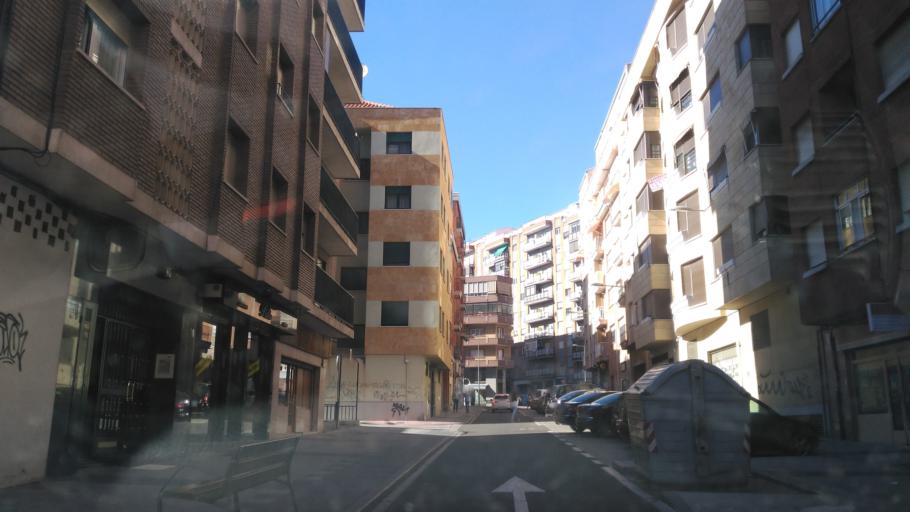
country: ES
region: Castille and Leon
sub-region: Provincia de Salamanca
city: Salamanca
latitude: 40.9717
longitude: -5.6514
